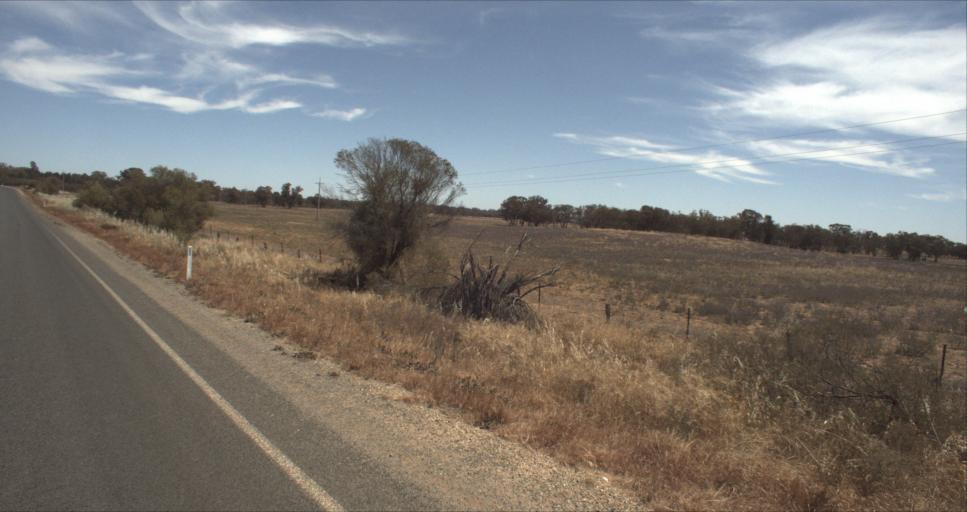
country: AU
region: New South Wales
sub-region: Leeton
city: Leeton
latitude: -34.6607
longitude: 146.4524
